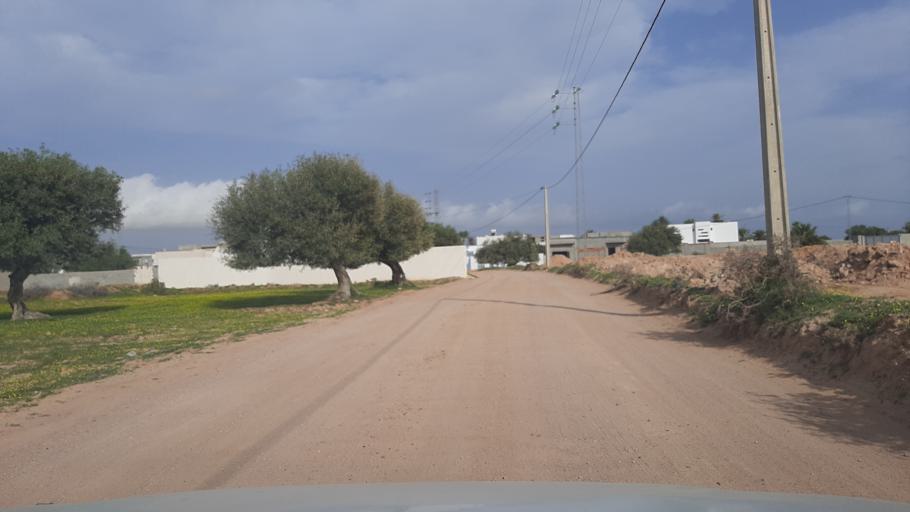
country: TN
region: Madanin
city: Midoun
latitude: 33.7999
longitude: 11.0276
